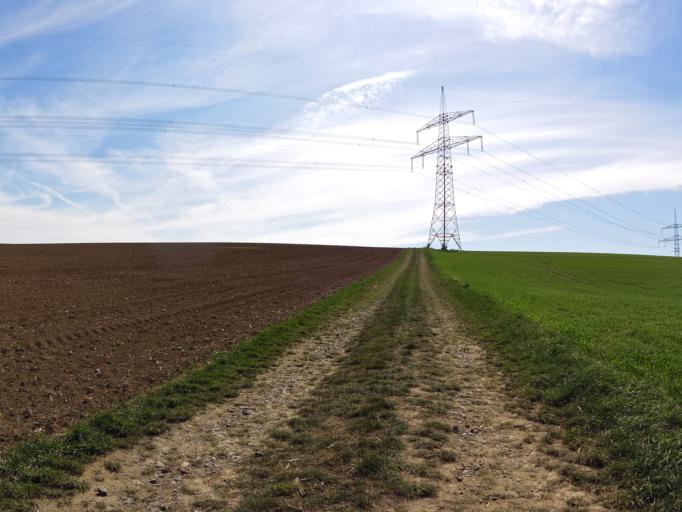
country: DE
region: Bavaria
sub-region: Regierungsbezirk Unterfranken
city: Rottendorf
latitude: 49.7899
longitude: 10.0522
